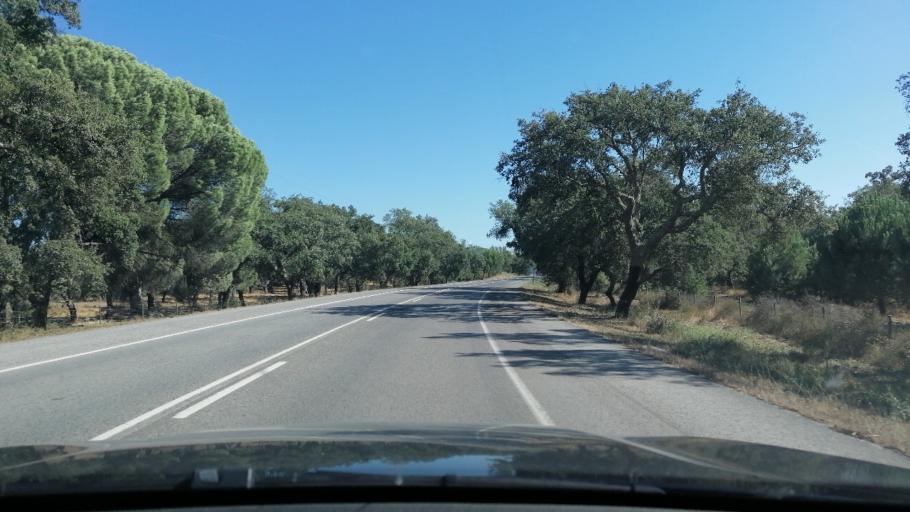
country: PT
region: Setubal
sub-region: Alcacer do Sal
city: Alcacer do Sal
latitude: 38.5541
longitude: -8.6510
